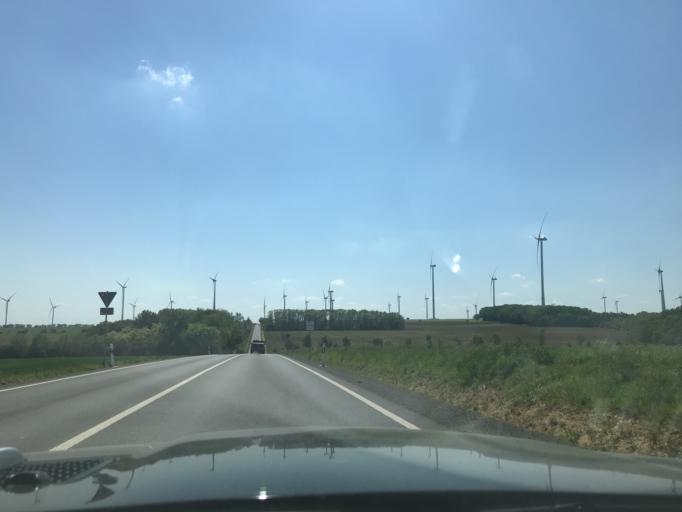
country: DE
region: Thuringia
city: Hochheim
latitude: 51.0519
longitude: 10.6546
